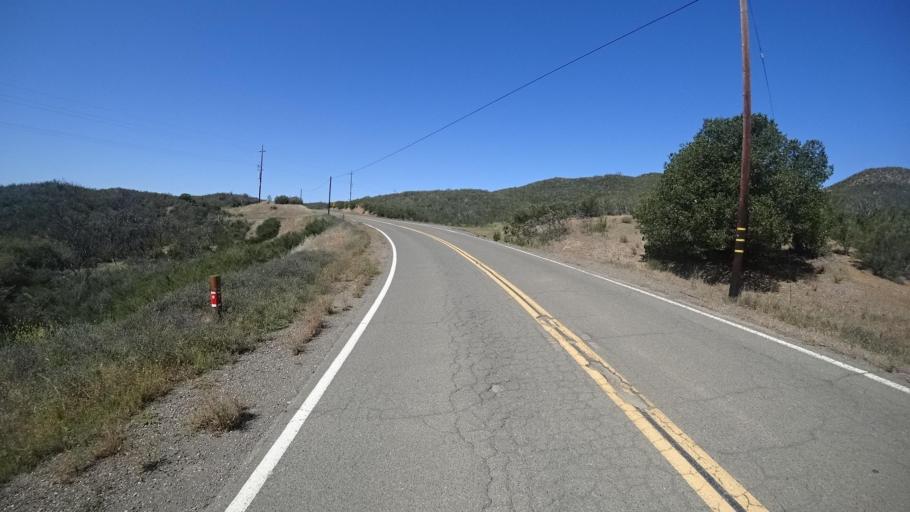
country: US
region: California
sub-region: Lake County
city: Hidden Valley Lake
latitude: 38.8861
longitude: -122.5117
